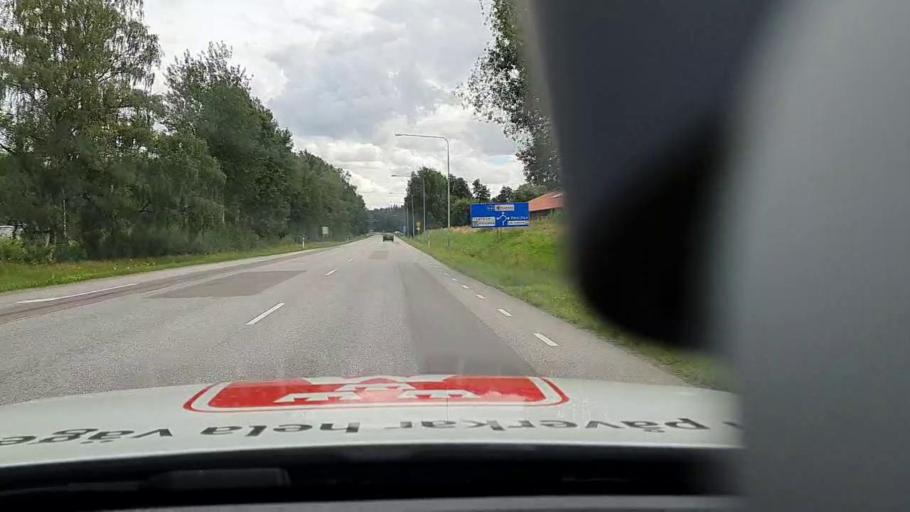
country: SE
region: Vaestra Goetaland
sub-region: Lidkopings Kommun
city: Lidkoping
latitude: 58.5224
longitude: 13.1129
